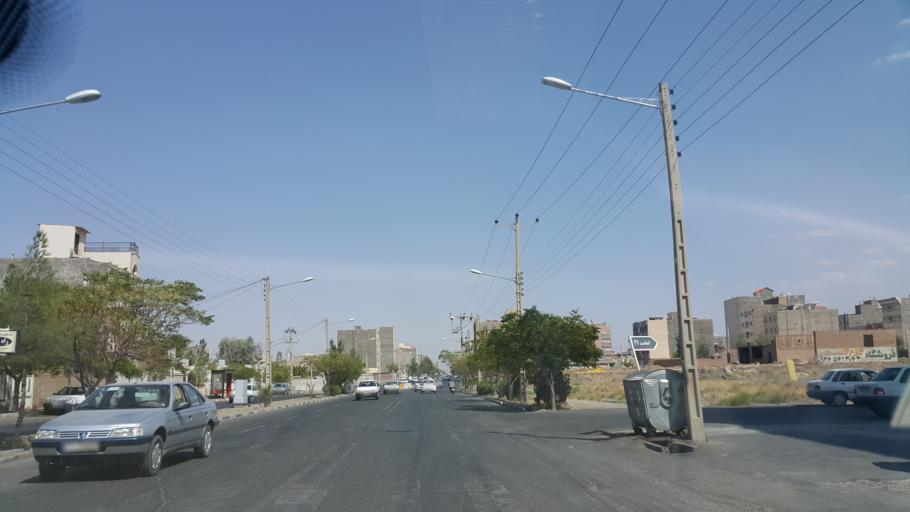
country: IR
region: Khorasan-e Jonubi
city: Birjand
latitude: 32.8460
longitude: 59.2094
